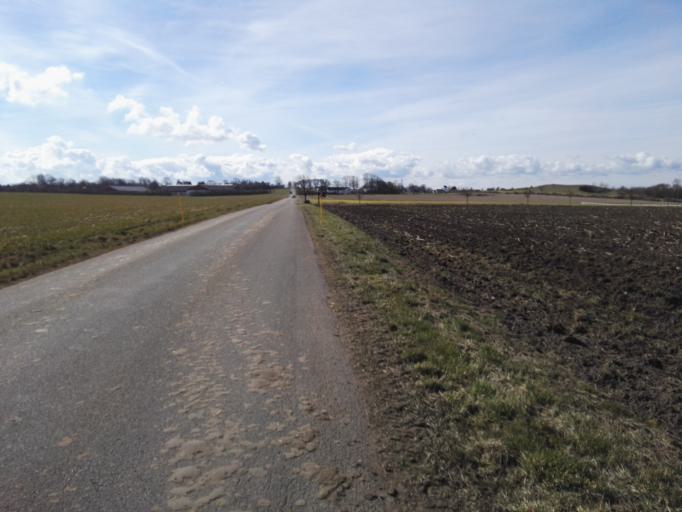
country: DK
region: Zealand
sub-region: Lejre Kommune
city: Ejby
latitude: 55.7733
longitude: 11.8196
